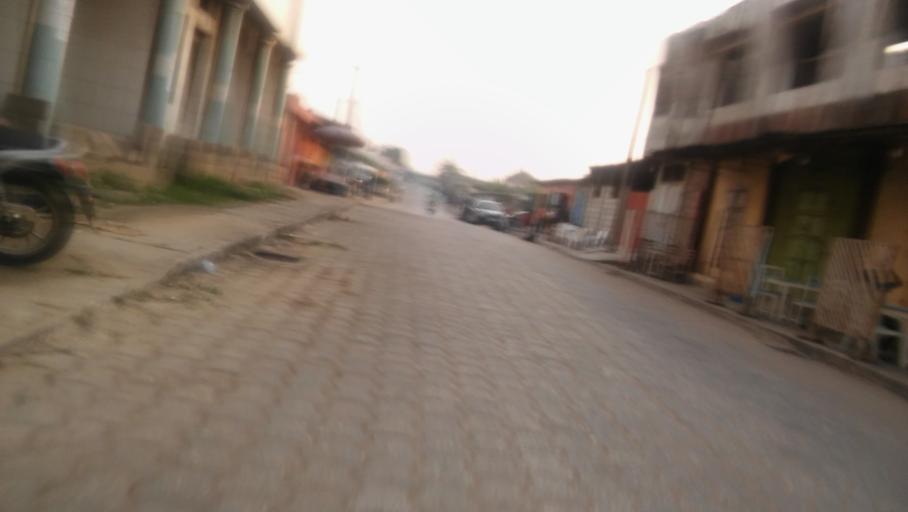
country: BJ
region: Atlantique
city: Abomey-Calavi
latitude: 6.3909
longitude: 2.3593
